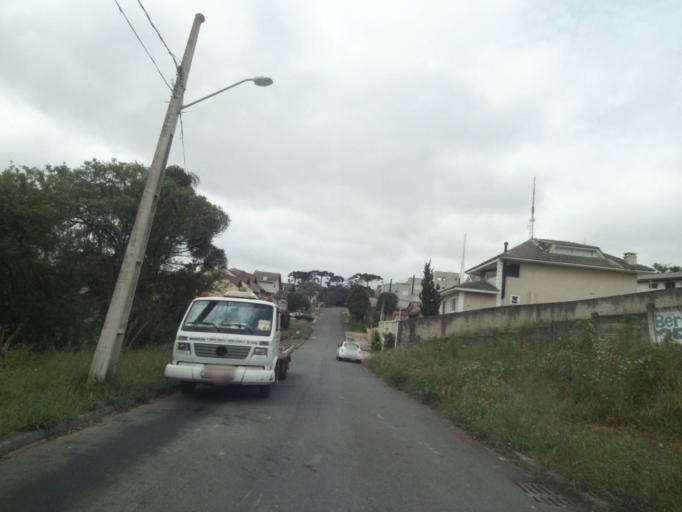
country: BR
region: Parana
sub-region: Curitiba
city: Curitiba
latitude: -25.3916
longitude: -49.2820
